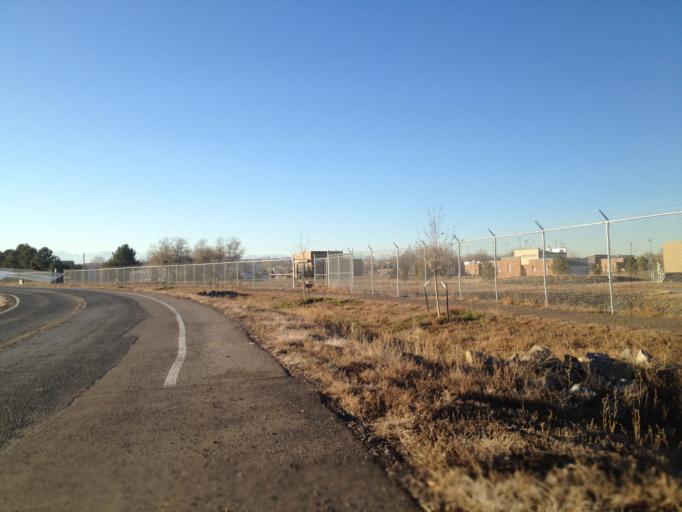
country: US
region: Colorado
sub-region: Boulder County
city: Louisville
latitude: 39.9784
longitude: -105.1206
